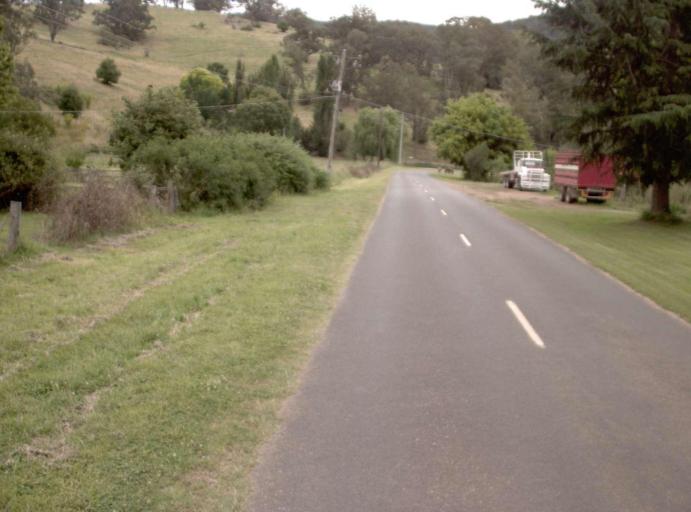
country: AU
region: Victoria
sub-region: East Gippsland
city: Bairnsdale
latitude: -37.4529
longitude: 147.2492
